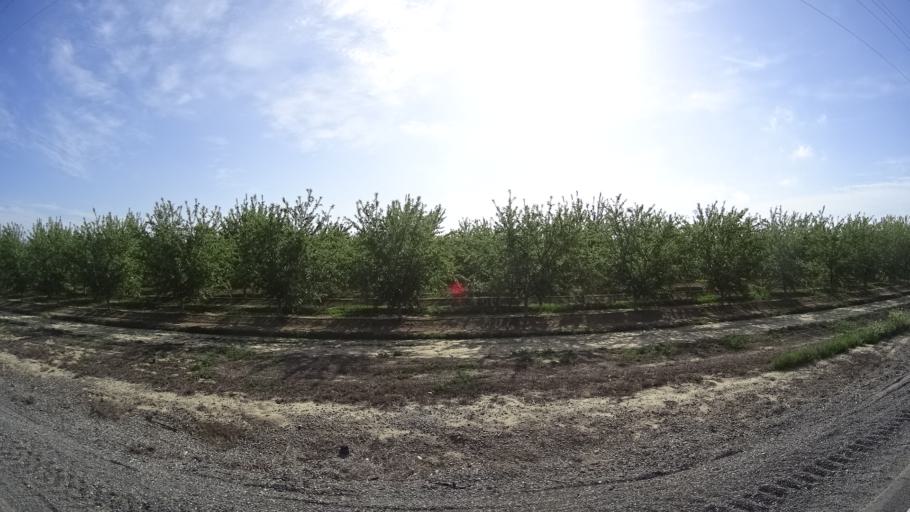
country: US
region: California
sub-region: Glenn County
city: Hamilton City
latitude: 39.6177
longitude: -122.0073
